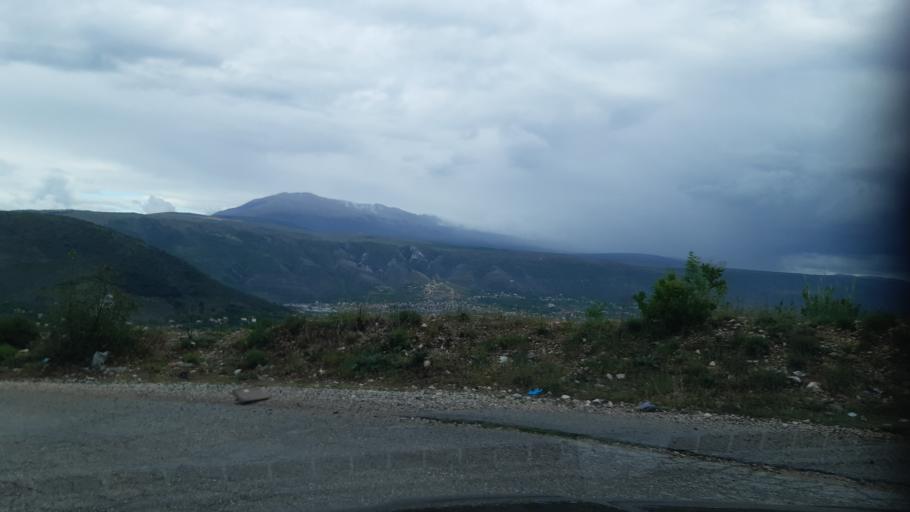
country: BA
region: Federation of Bosnia and Herzegovina
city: Rodoc
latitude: 43.3041
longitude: 17.7815
